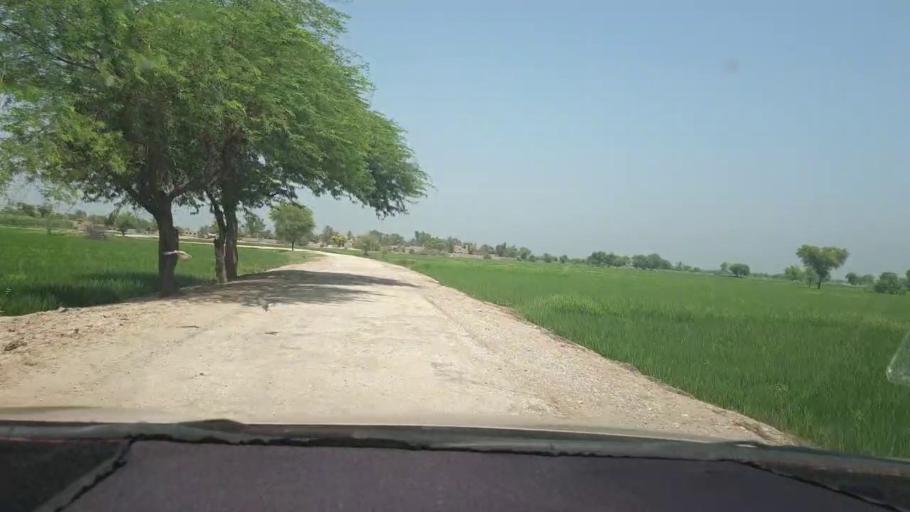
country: PK
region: Sindh
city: Kambar
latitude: 27.6210
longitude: 68.0535
